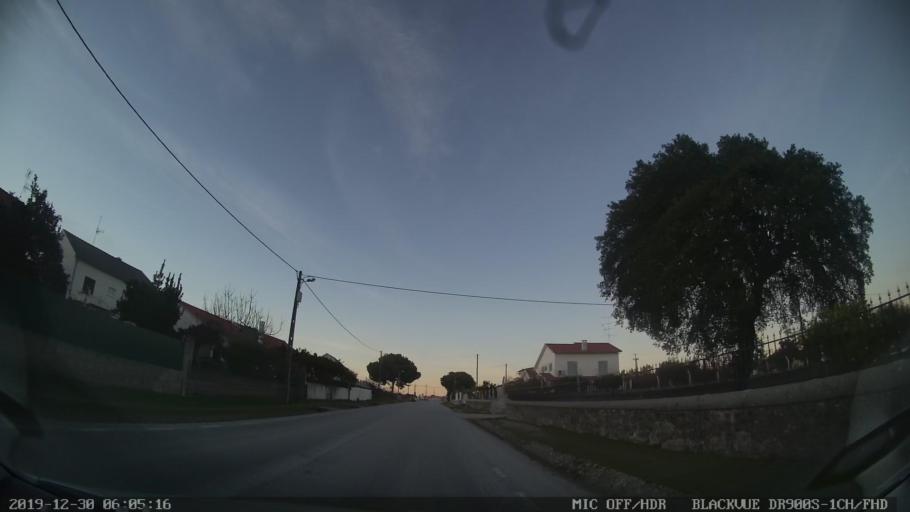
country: PT
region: Castelo Branco
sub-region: Penamacor
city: Penamacor
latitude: 40.0893
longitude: -7.2356
